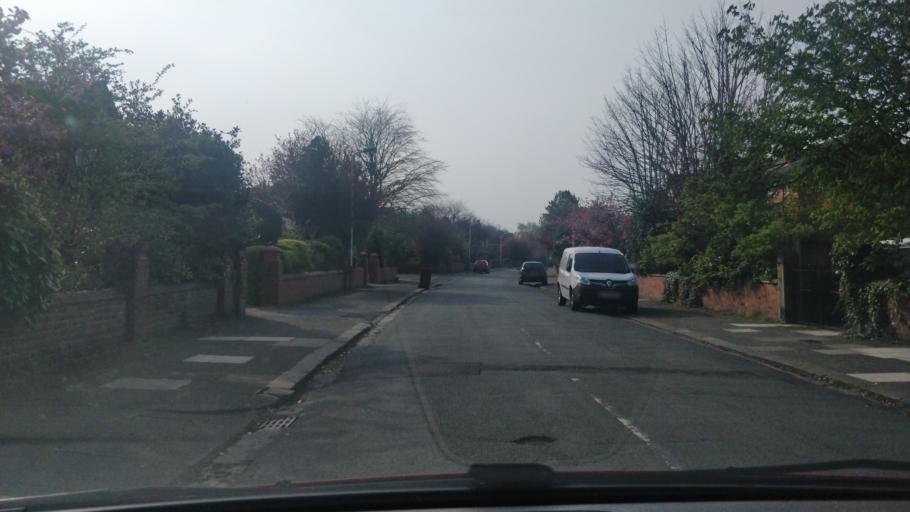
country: GB
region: England
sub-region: Sefton
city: Formby
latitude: 53.6003
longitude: -3.0397
